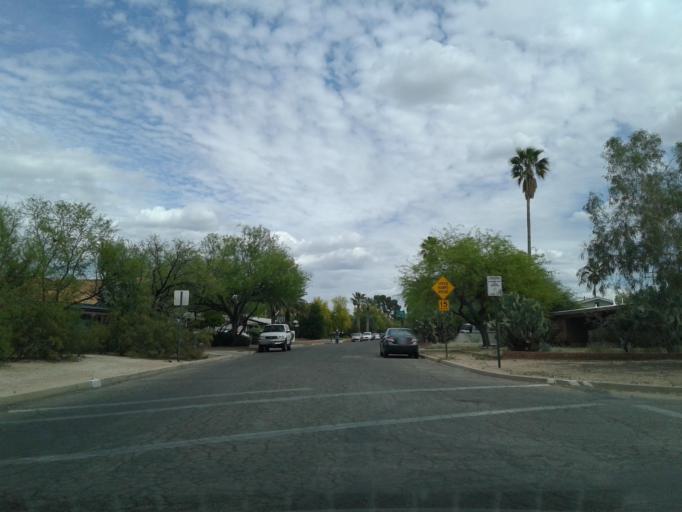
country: US
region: Arizona
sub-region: Pima County
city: Tucson
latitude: 32.2325
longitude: -110.9221
